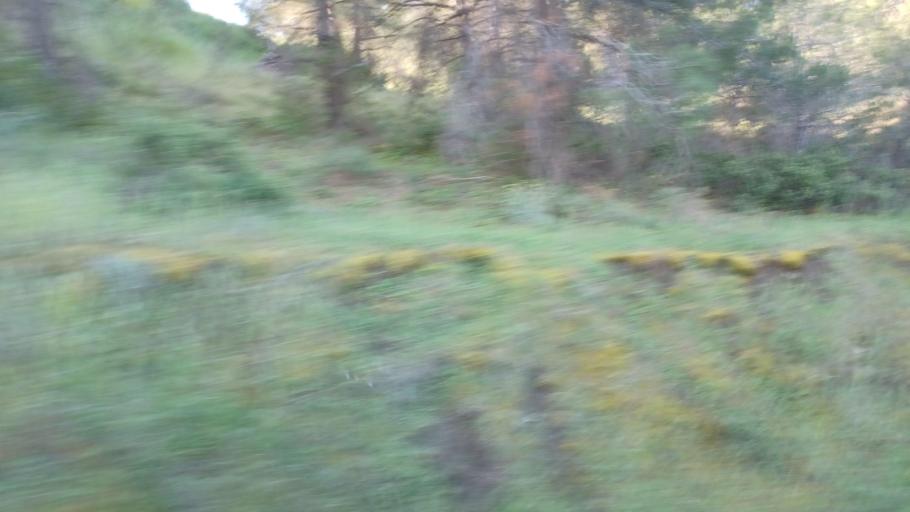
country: CY
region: Lefkosia
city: Peristerona
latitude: 35.0301
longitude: 33.0527
